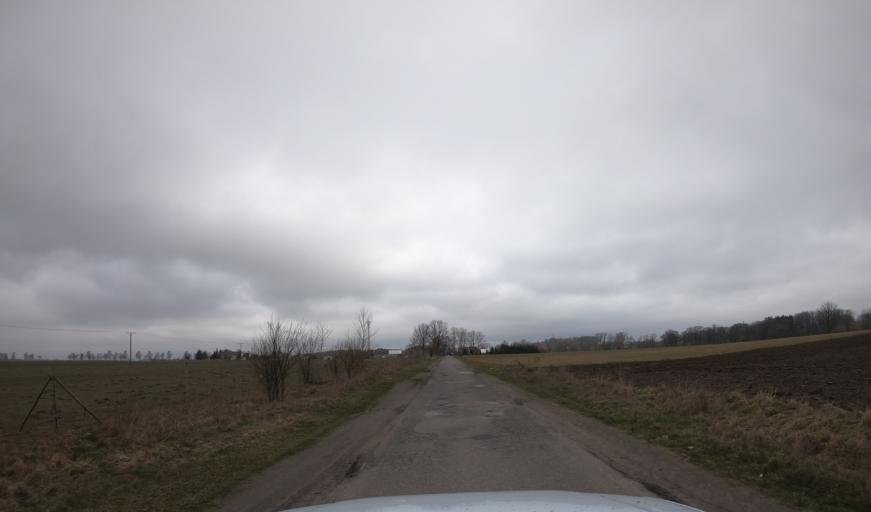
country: PL
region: West Pomeranian Voivodeship
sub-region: Powiat gryficki
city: Cerkwica
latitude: 53.9986
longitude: 15.1044
